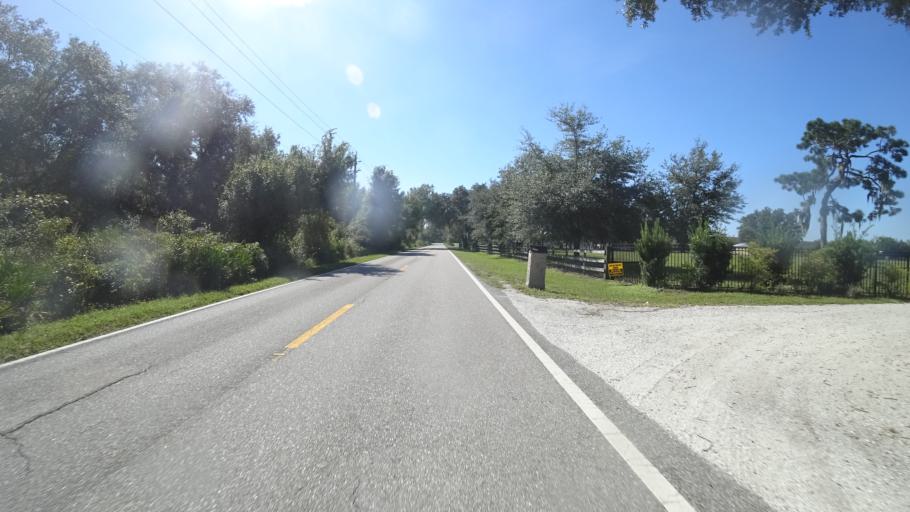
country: US
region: Florida
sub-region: Sarasota County
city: Lake Sarasota
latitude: 27.3242
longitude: -82.2694
